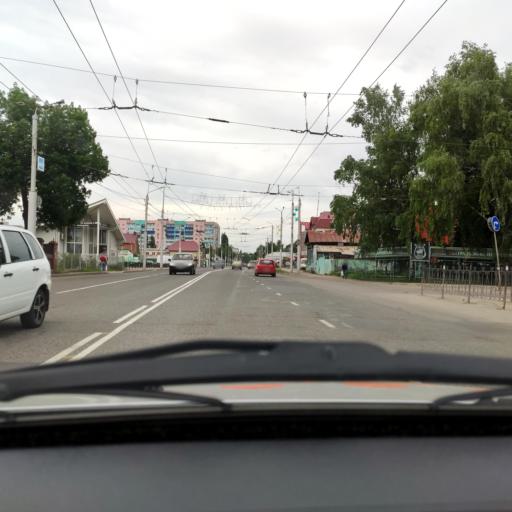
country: RU
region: Bashkortostan
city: Sterlitamak
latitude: 53.6148
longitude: 55.9566
